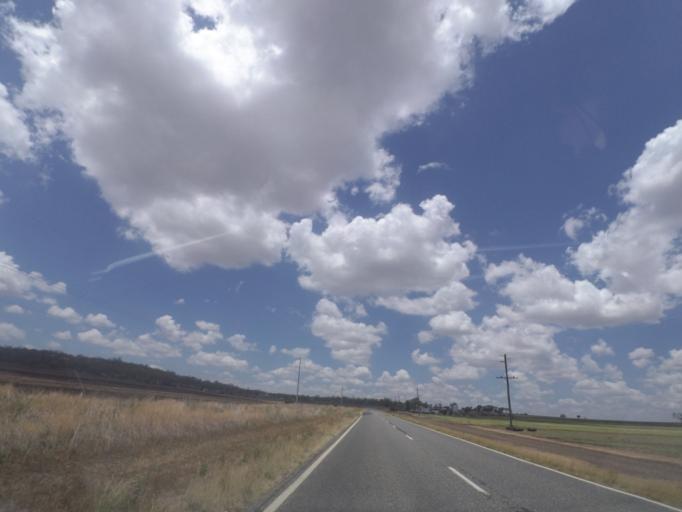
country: AU
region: Queensland
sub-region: Toowoomba
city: Top Camp
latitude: -27.8750
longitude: 151.9651
